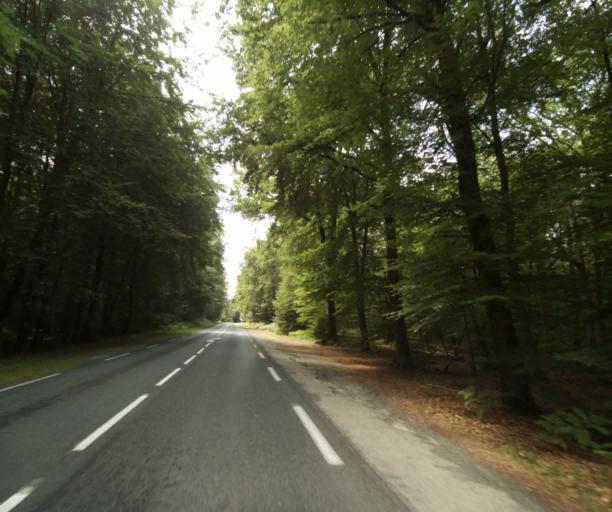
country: FR
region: Ile-de-France
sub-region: Departement de Seine-et-Marne
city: Barbizon
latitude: 48.4132
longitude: 2.6475
